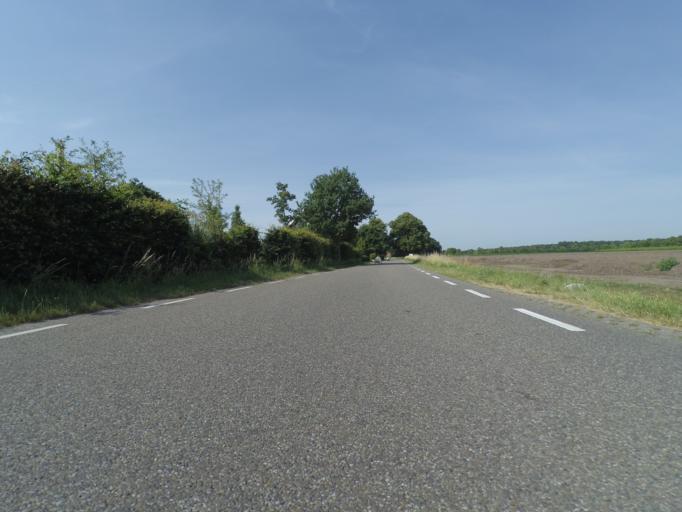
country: NL
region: North Brabant
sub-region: Gemeente Bergen op Zoom
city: Bergen op Zoom
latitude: 51.5247
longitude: 4.3283
